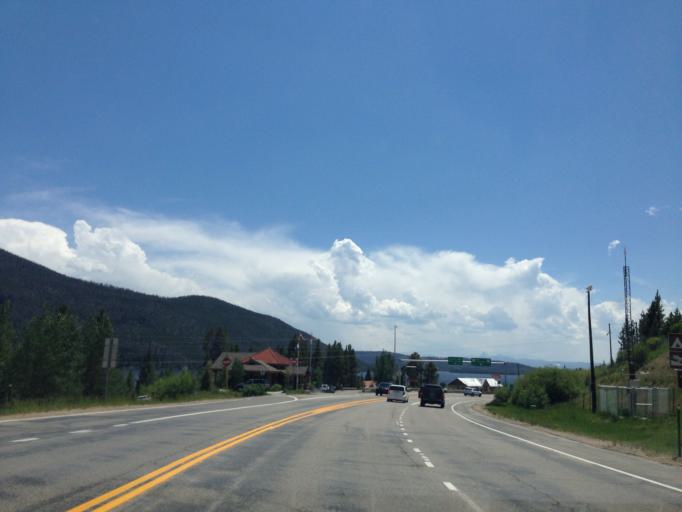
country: US
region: Colorado
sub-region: Grand County
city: Granby
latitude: 40.2526
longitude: -105.8350
